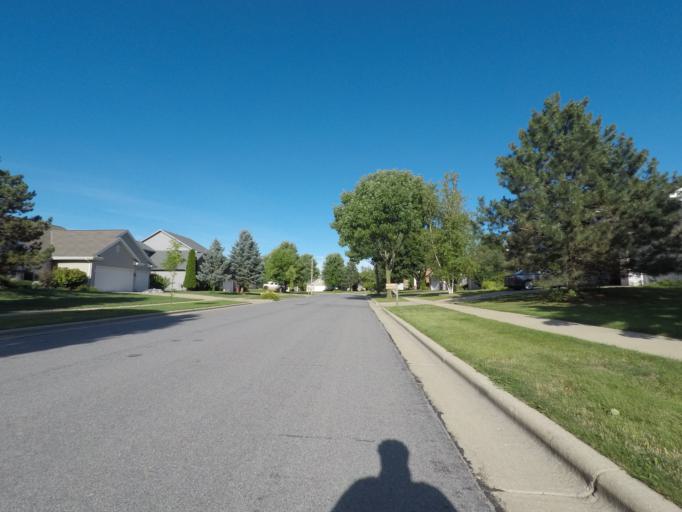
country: US
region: Wisconsin
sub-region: Dane County
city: Middleton
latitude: 43.0690
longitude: -89.5290
